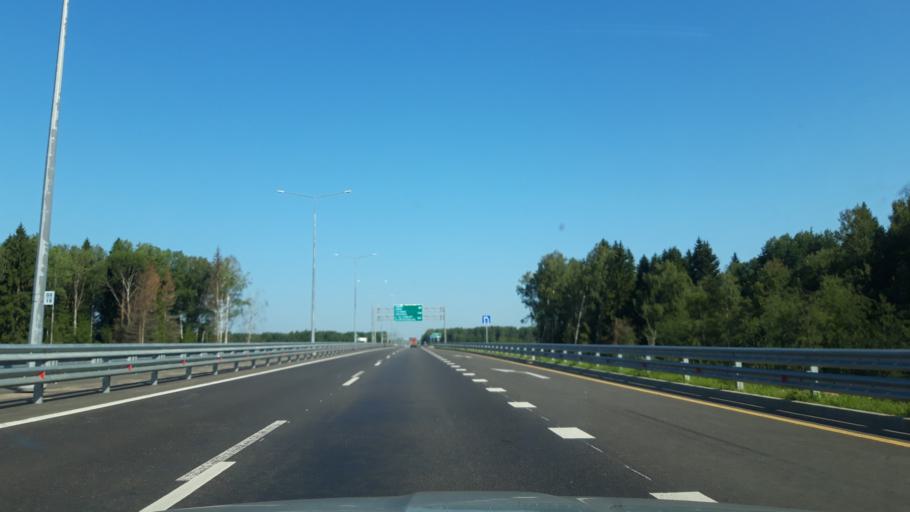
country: RU
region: Moskovskaya
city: Vysokovsk
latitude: 56.3614
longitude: 36.6050
